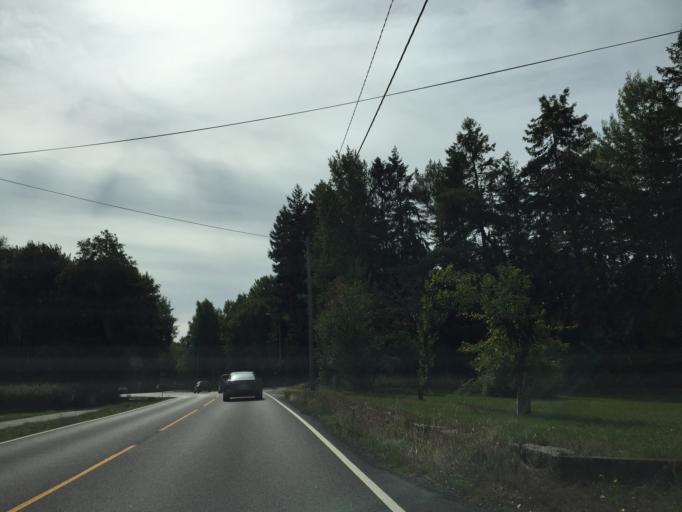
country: NO
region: Ostfold
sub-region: Fredrikstad
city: Fredrikstad
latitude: 59.1547
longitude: 10.9352
